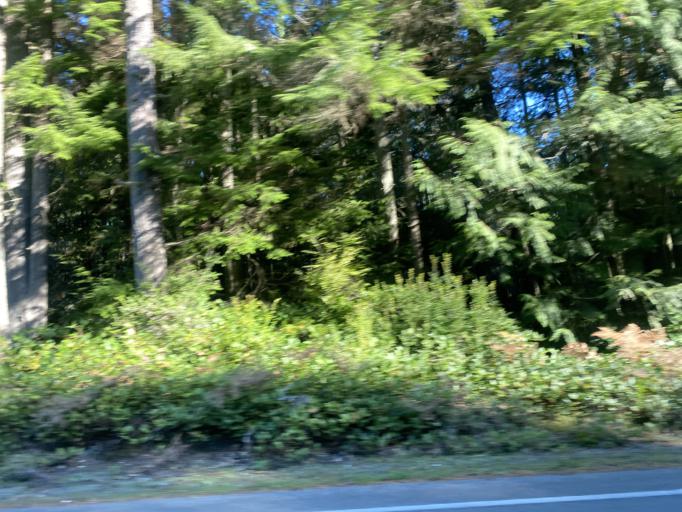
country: US
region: Washington
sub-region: Island County
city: Langley
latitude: 48.0050
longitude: -122.4248
